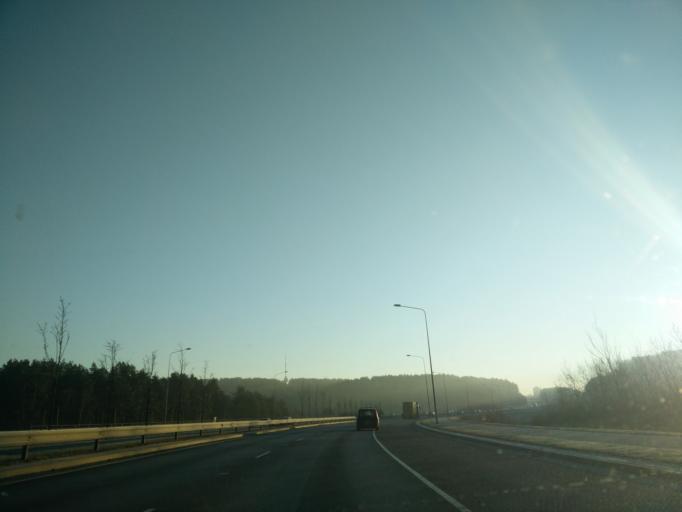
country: LT
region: Vilnius County
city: Lazdynai
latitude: 54.6689
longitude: 25.1777
